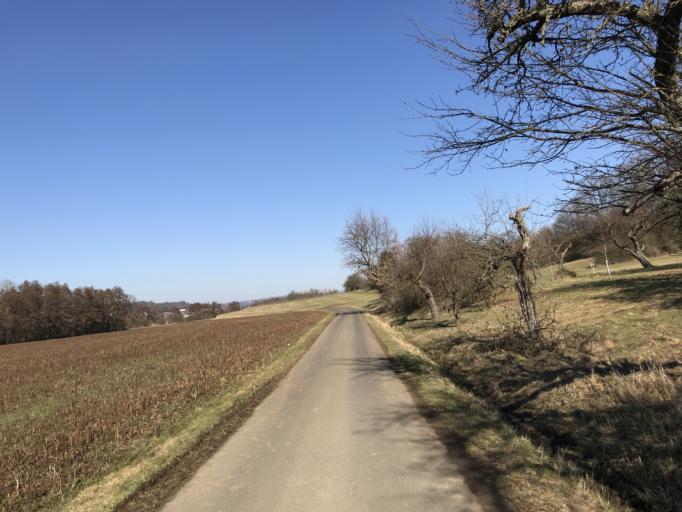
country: DE
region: Hesse
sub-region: Regierungsbezirk Darmstadt
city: Nidda
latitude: 50.3951
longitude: 8.9959
